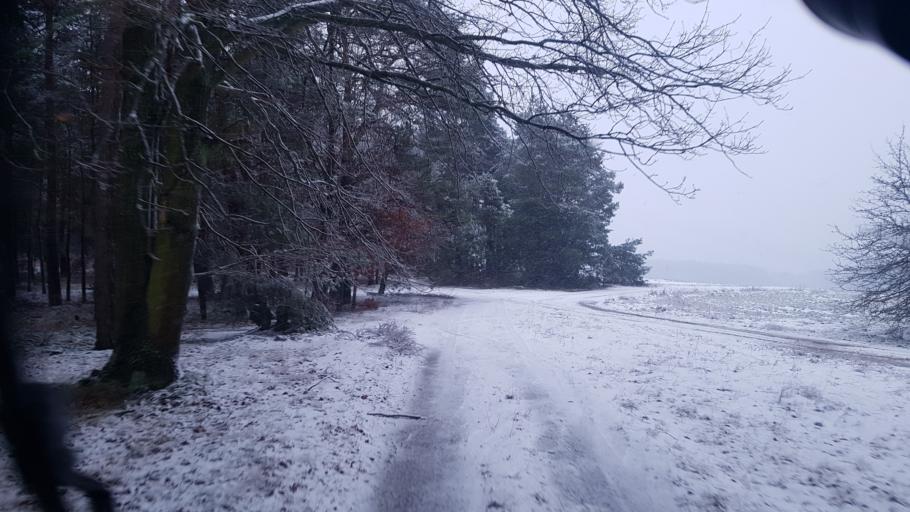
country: DE
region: Brandenburg
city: Schenkendobern
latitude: 51.9044
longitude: 14.5811
